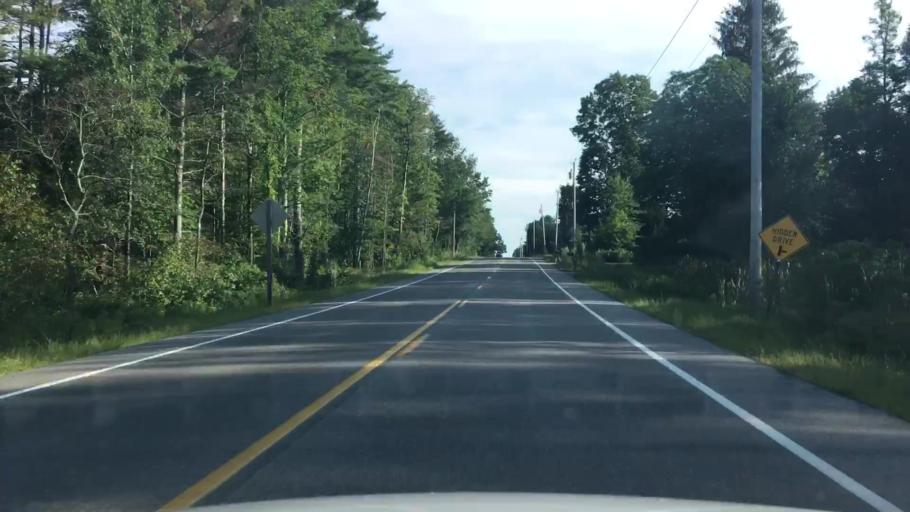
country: US
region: Maine
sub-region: Cumberland County
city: North Windham
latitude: 43.8153
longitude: -70.4413
